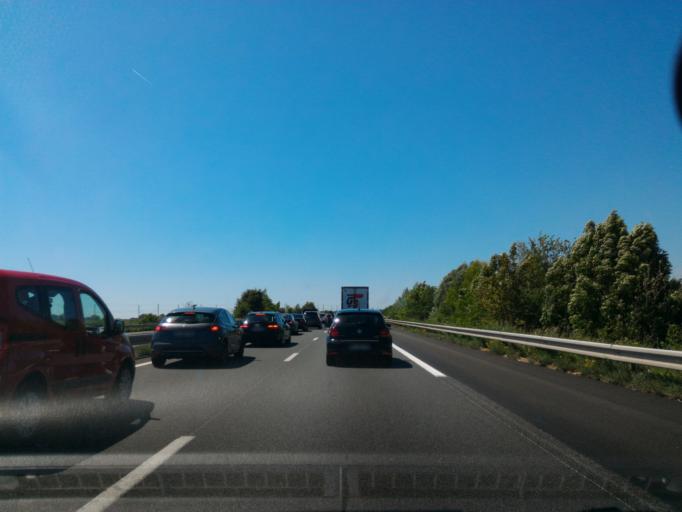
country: FR
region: Centre
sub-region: Departement d'Indre-et-Loire
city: La Celle-Saint-Avant
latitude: 47.0510
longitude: 0.5875
